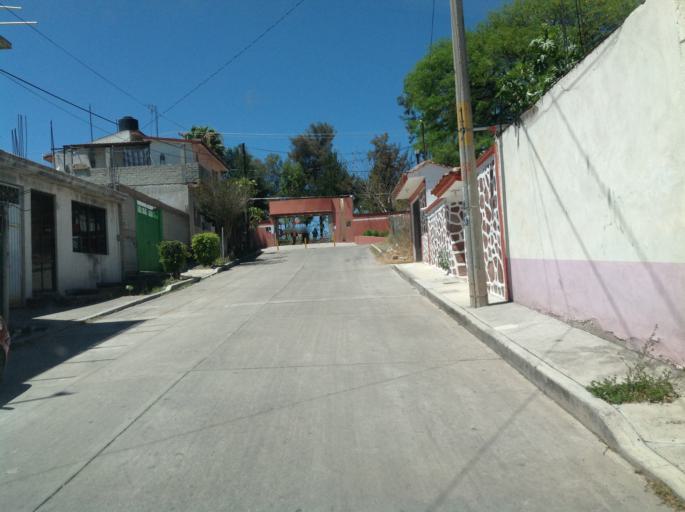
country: MX
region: Oaxaca
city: Ciudad de Huajuapam de Leon
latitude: 17.8141
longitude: -97.7792
